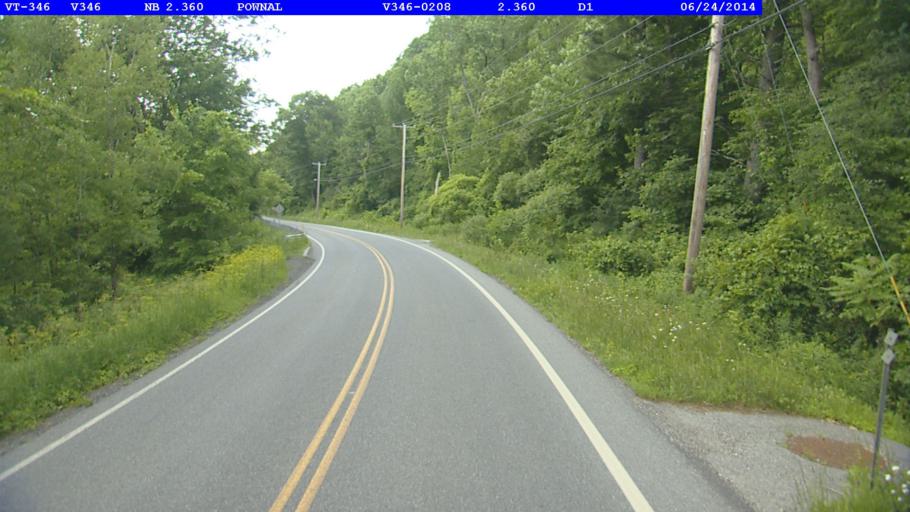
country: US
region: Massachusetts
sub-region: Berkshire County
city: Williamstown
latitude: 42.7916
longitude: -73.2553
